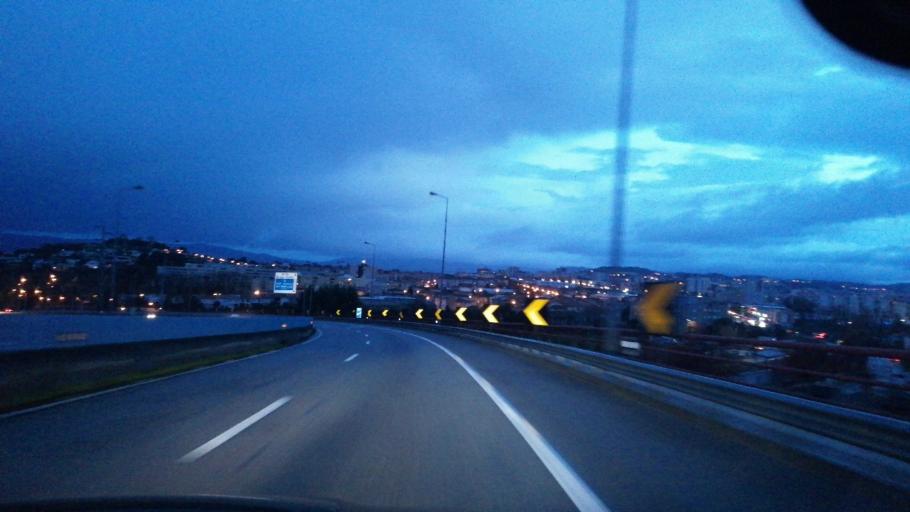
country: PT
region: Braga
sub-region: Braga
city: Braga
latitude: 41.5295
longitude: -8.4432
